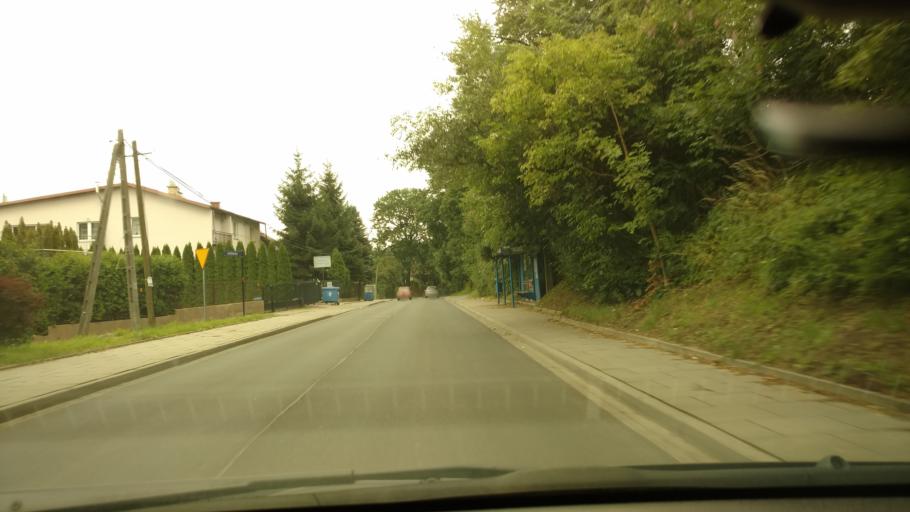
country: PL
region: Lesser Poland Voivodeship
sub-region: Powiat krakowski
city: Zielonki
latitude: 50.1052
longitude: 19.9442
